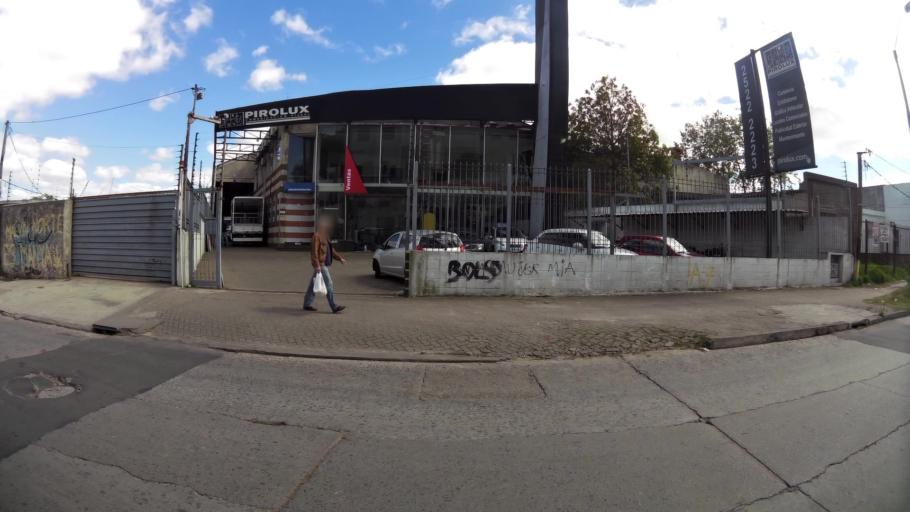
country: UY
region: Canelones
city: Paso de Carrasco
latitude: -34.8704
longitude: -56.1121
